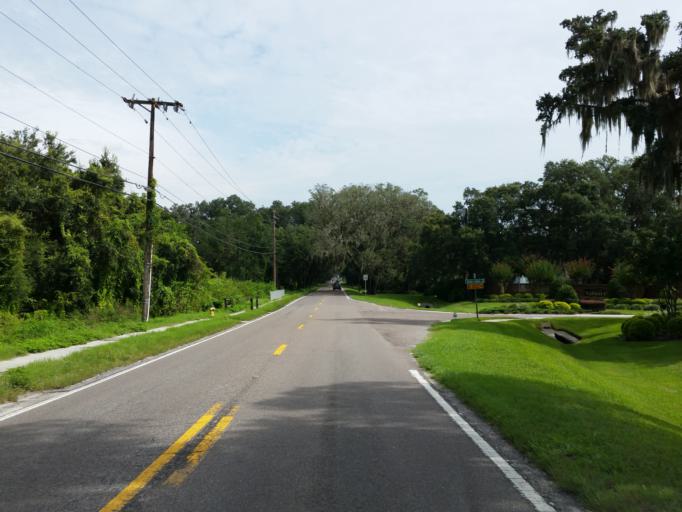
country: US
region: Florida
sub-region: Hillsborough County
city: Valrico
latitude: 27.9545
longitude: -82.2528
